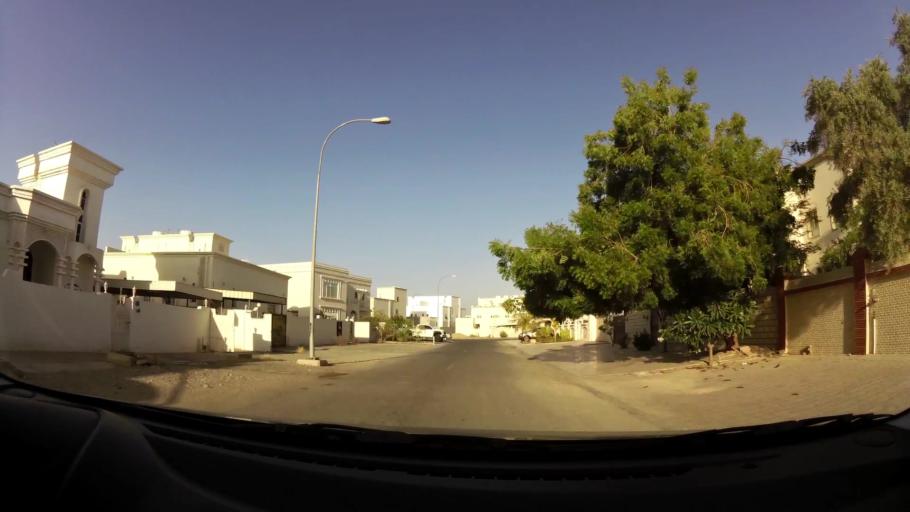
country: OM
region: Muhafazat Masqat
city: As Sib al Jadidah
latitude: 23.6125
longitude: 58.2191
